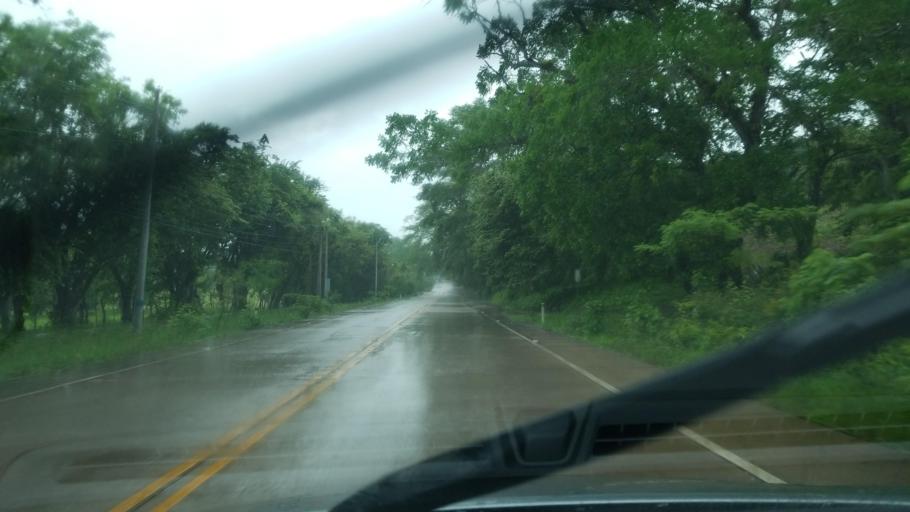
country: HN
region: Copan
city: Copan
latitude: 14.8455
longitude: -89.1382
